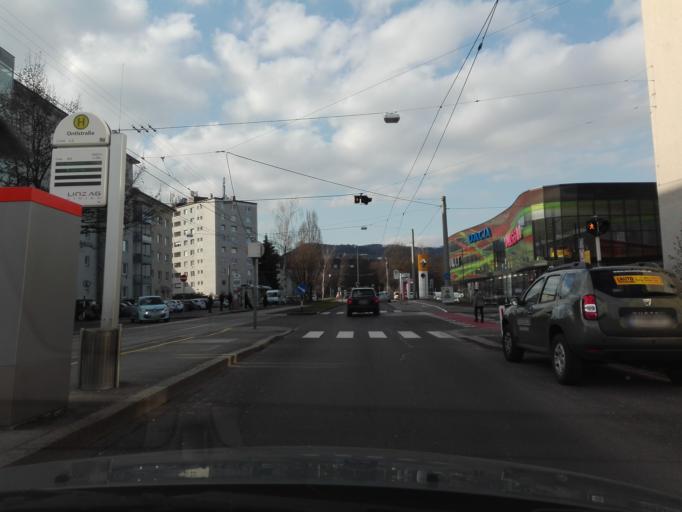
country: AT
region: Upper Austria
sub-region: Linz Stadt
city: Linz
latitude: 48.3224
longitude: 14.2856
